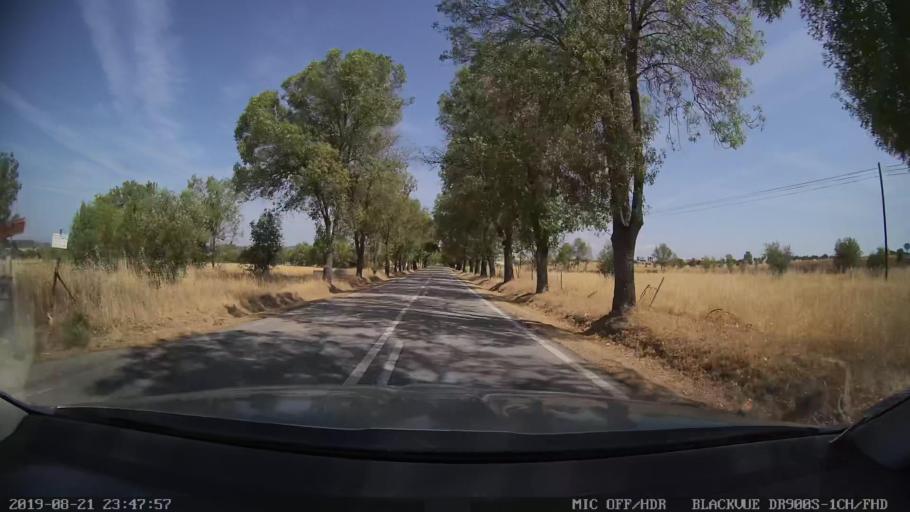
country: PT
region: Castelo Branco
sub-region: Idanha-A-Nova
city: Idanha-a-Nova
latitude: 39.8579
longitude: -7.2594
